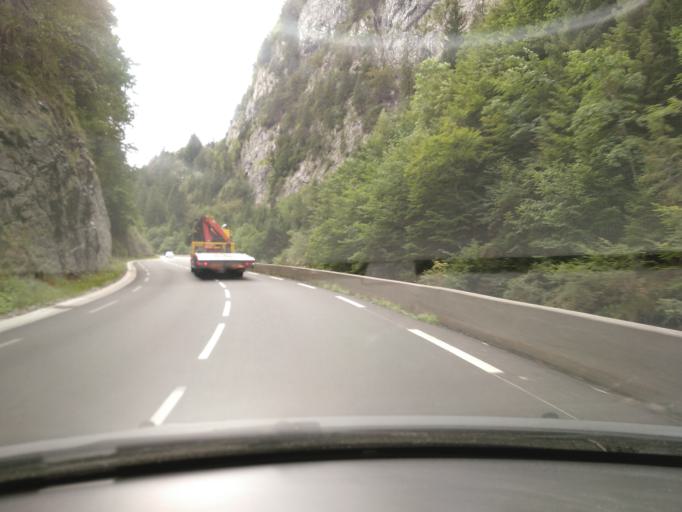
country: FR
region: Rhone-Alpes
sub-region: Departement de la Haute-Savoie
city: Saint-Jean-de-Sixt
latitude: 45.9345
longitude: 6.4003
